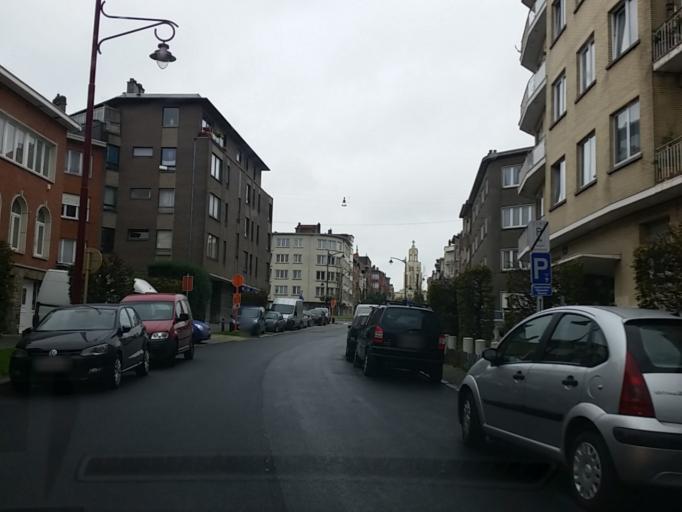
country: BE
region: Flanders
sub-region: Provincie Vlaams-Brabant
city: Drogenbos
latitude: 50.8123
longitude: 4.3352
